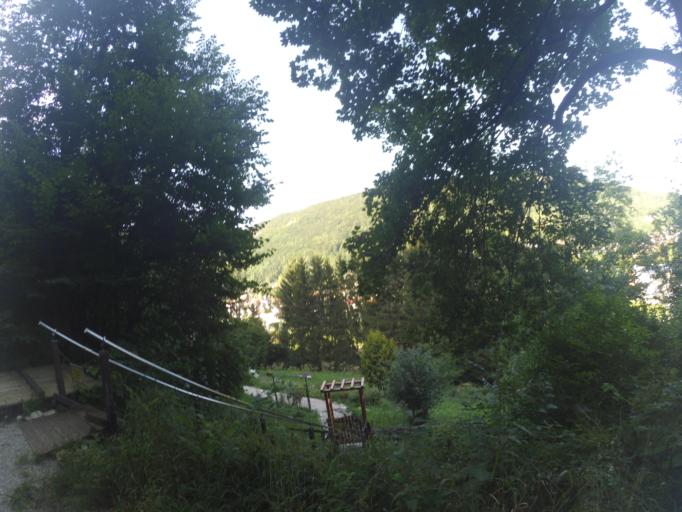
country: DE
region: Baden-Wuerttemberg
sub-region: Tuebingen Region
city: Bad Urach
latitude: 48.4942
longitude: 9.3846
